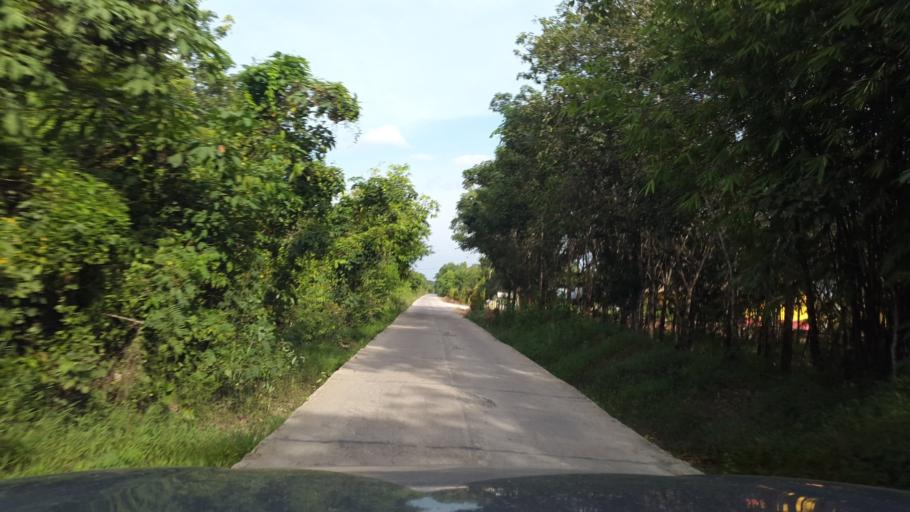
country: ID
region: South Sumatra
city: Glumbang
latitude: -3.4207
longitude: 104.5145
